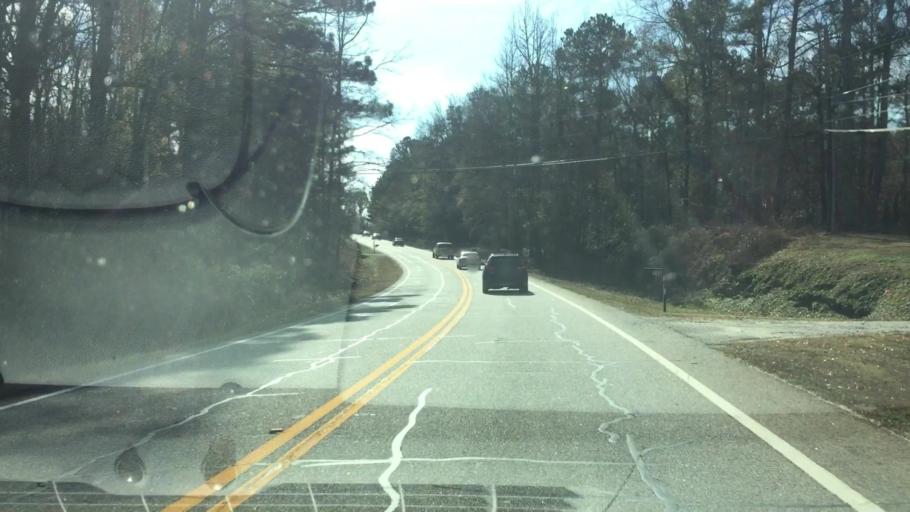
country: US
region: Georgia
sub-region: Henry County
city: McDonough
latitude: 33.4725
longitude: -84.1393
